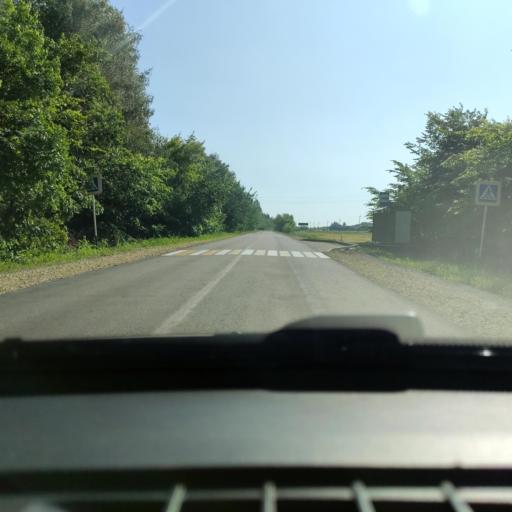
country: RU
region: Voronezj
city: Anna
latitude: 51.6306
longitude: 40.3491
